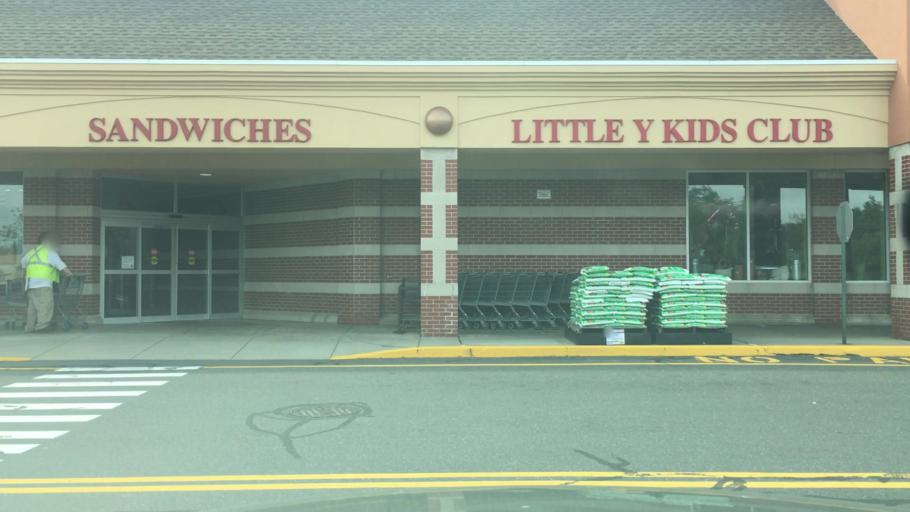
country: US
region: Connecticut
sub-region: Hartford County
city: Manchester
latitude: 41.8103
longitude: -72.5141
